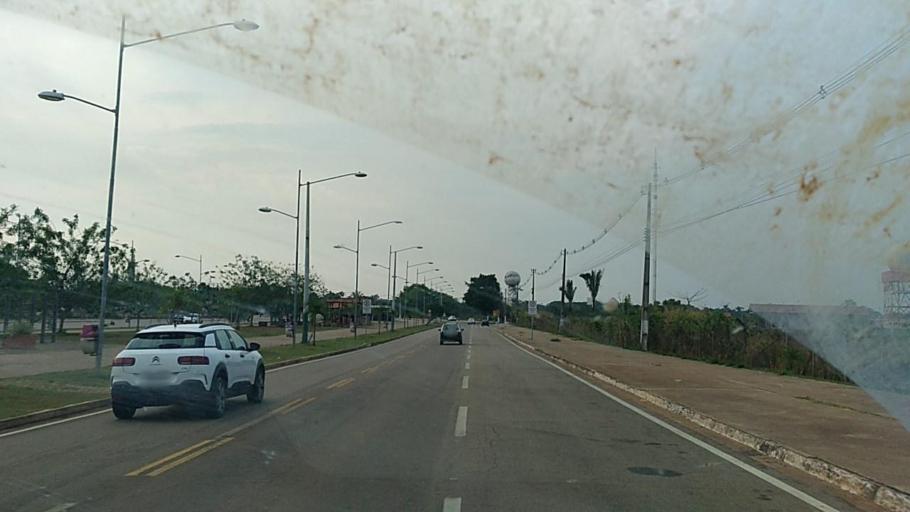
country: BR
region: Rondonia
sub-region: Porto Velho
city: Porto Velho
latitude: -8.7174
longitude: -63.8948
